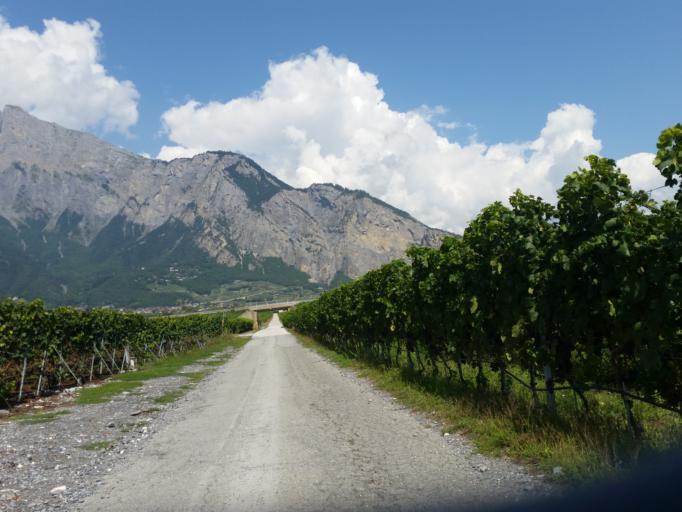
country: CH
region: Valais
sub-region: Martigny District
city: Riddes
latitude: 46.1799
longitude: 7.2201
